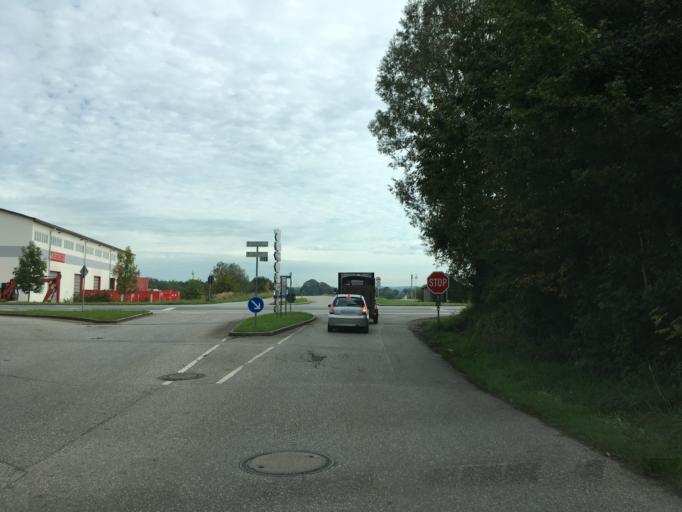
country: DE
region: Bavaria
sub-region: Upper Bavaria
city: Wasserburg am Inn
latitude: 48.0443
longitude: 12.2259
